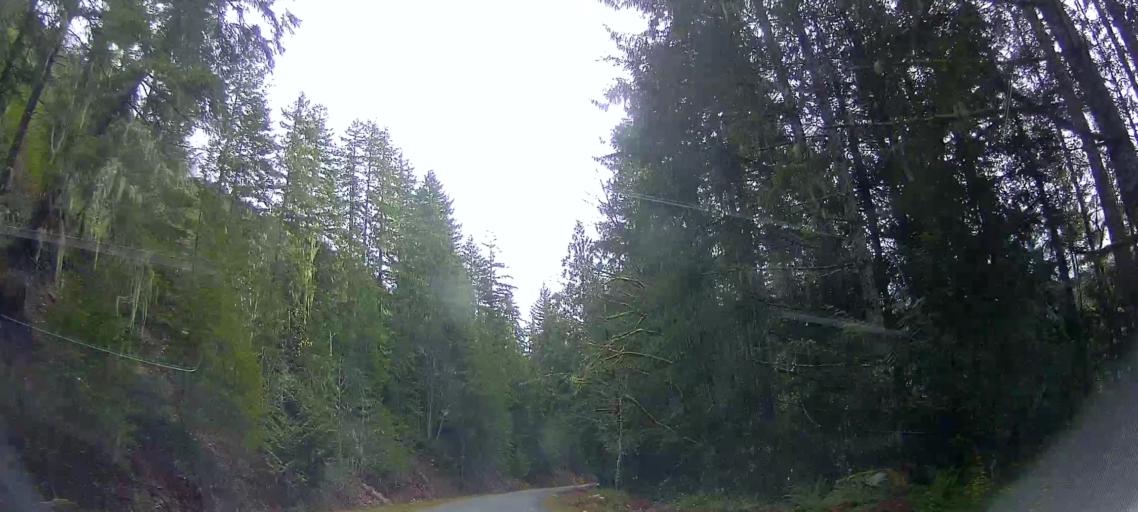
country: US
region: Washington
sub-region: Snohomish County
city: Darrington
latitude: 48.5288
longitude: -121.3921
